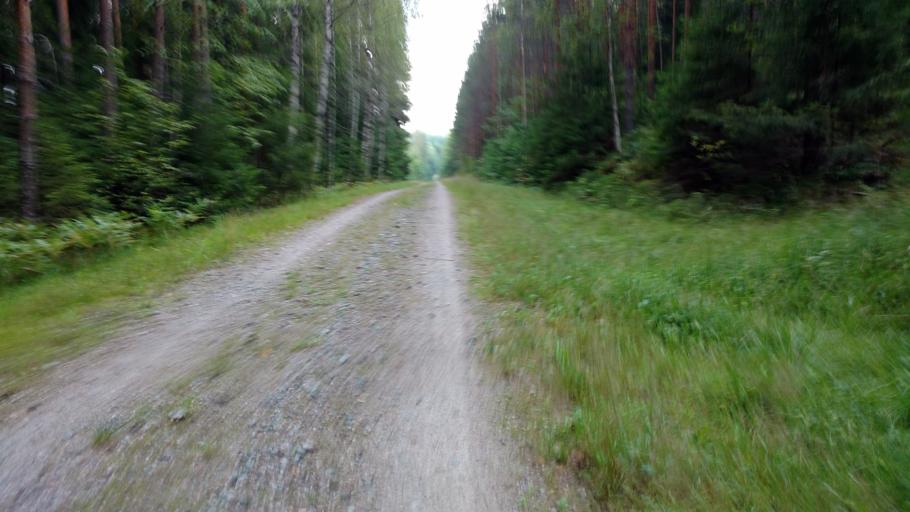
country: FI
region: Varsinais-Suomi
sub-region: Salo
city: Pertteli
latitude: 60.3964
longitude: 23.2216
